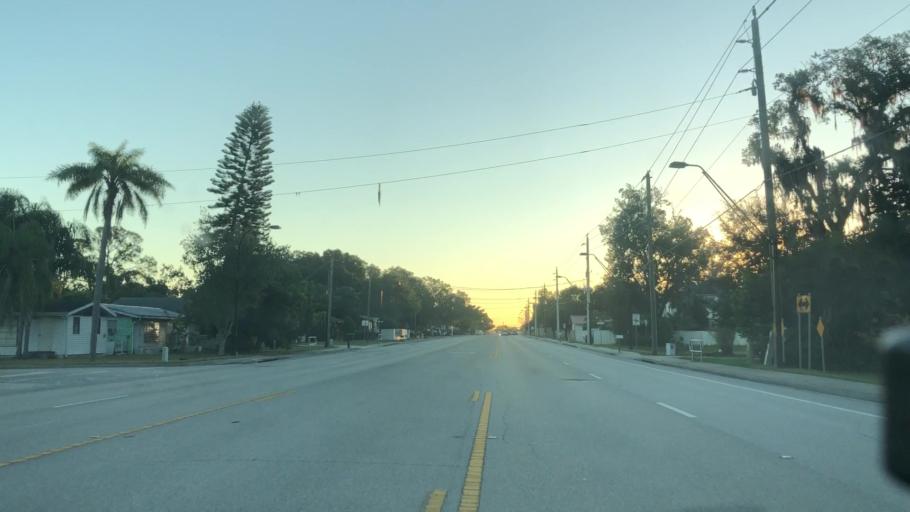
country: US
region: Florida
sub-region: Sarasota County
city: Fruitville
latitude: 27.3231
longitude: -82.4587
